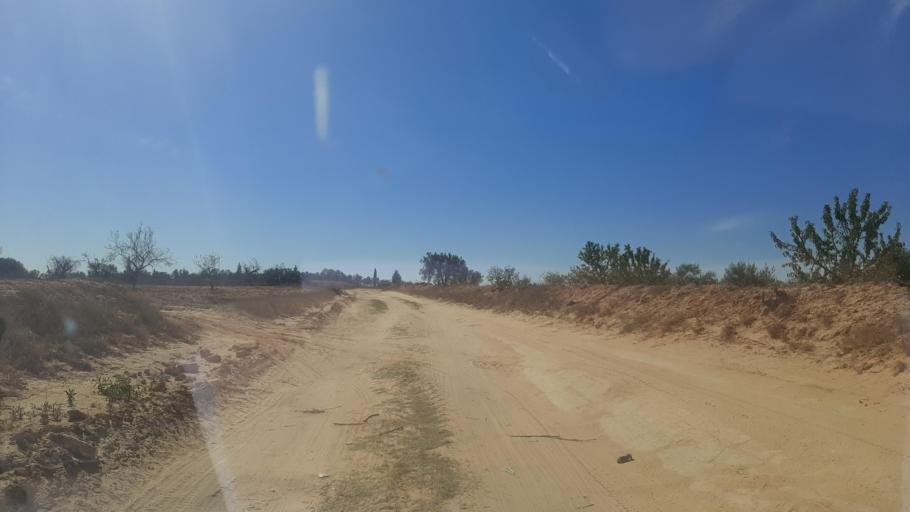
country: TN
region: Safaqis
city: Sfax
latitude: 34.8317
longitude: 10.5566
